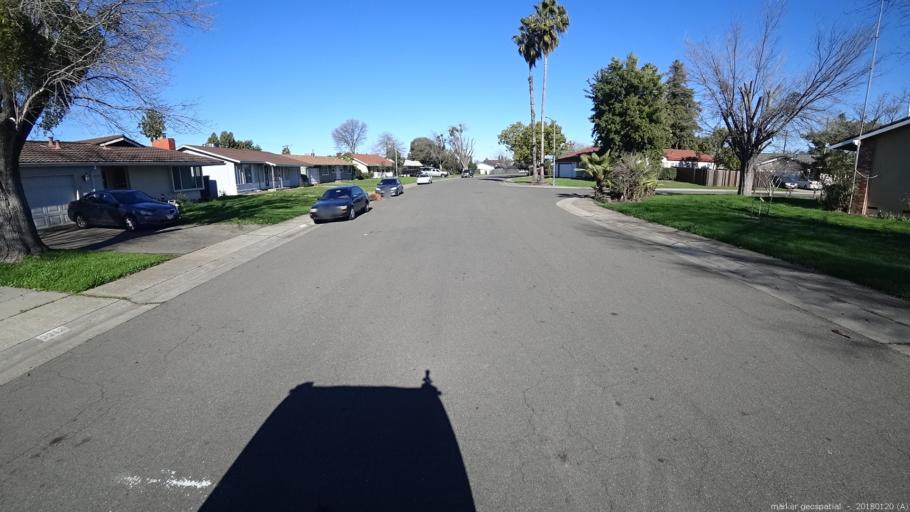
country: US
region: California
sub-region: Sacramento County
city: La Riviera
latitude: 38.5661
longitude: -121.3268
